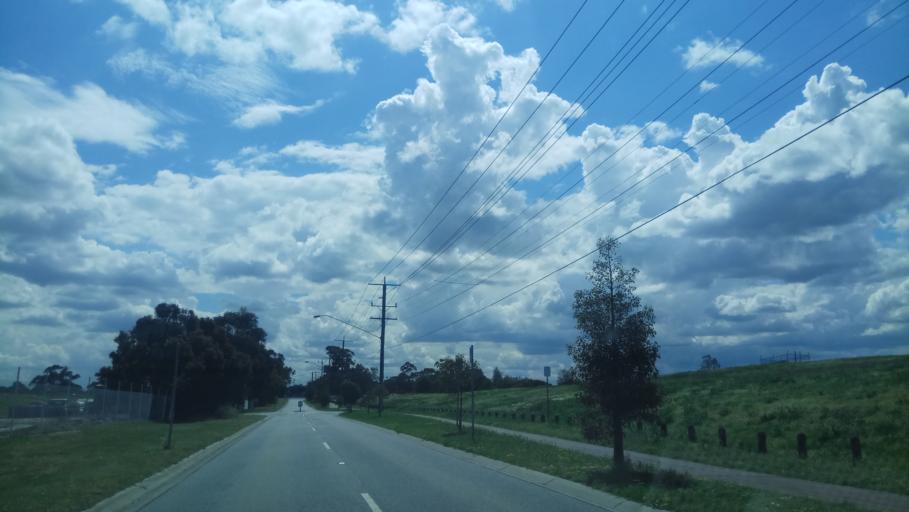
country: AU
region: Victoria
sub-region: Greater Dandenong
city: Springvale South
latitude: -37.9703
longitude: 145.1419
